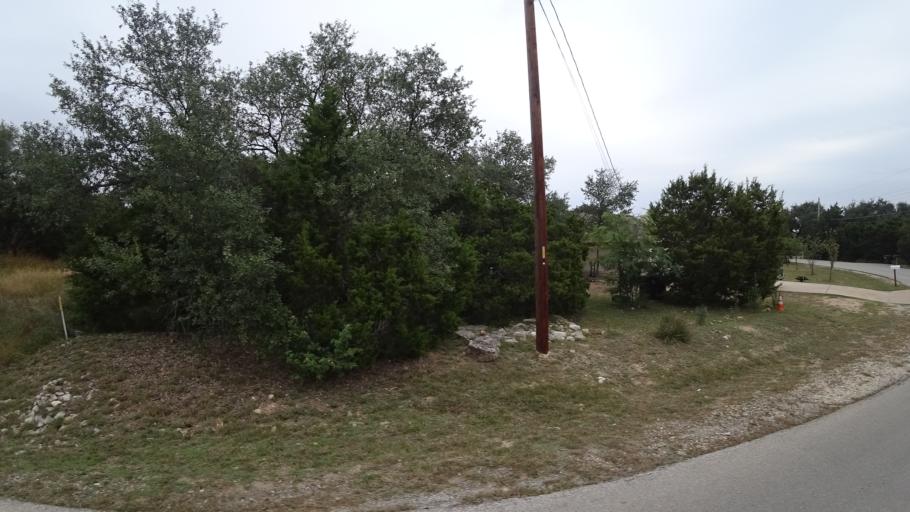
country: US
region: Texas
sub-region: Travis County
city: Hudson Bend
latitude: 30.3723
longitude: -97.9246
